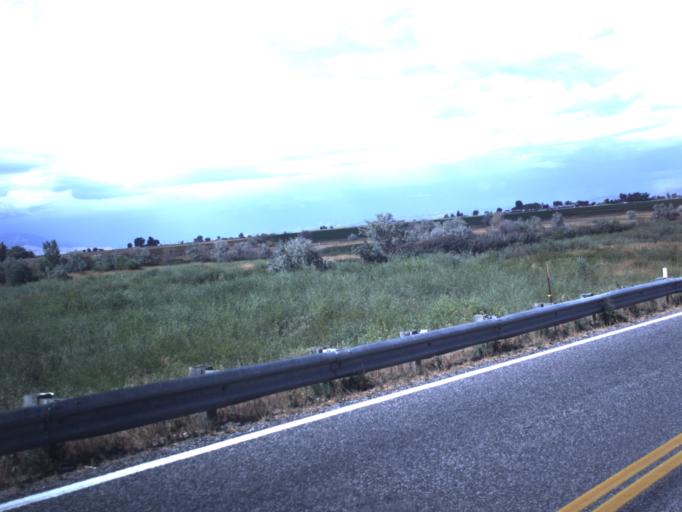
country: US
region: Utah
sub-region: Cache County
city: Lewiston
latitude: 41.9208
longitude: -111.9088
